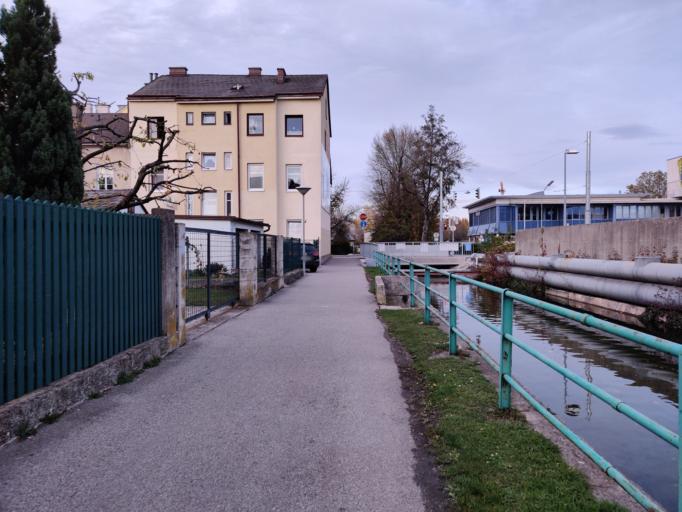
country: AT
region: Lower Austria
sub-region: Sankt Polten Stadt
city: Sankt Poelten
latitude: 48.2095
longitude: 15.6302
